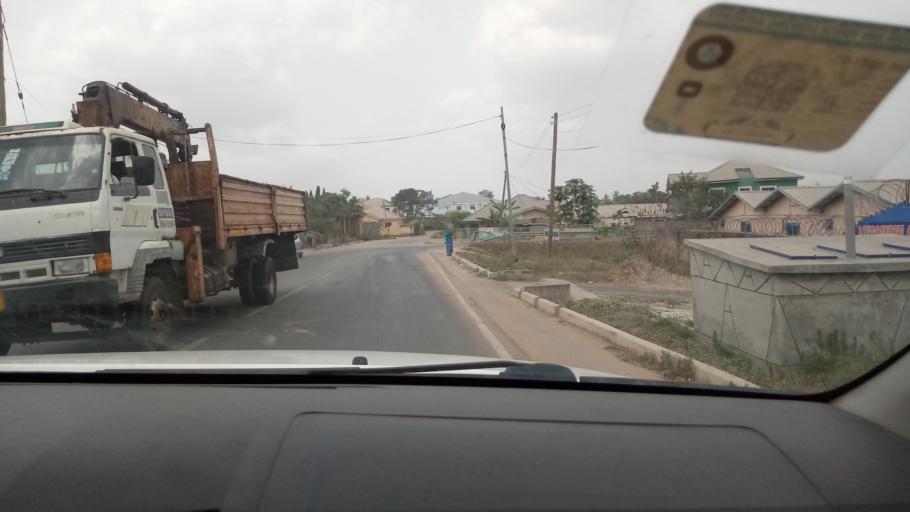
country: GH
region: Central
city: Kasoa
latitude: 5.5281
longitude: -0.4483
